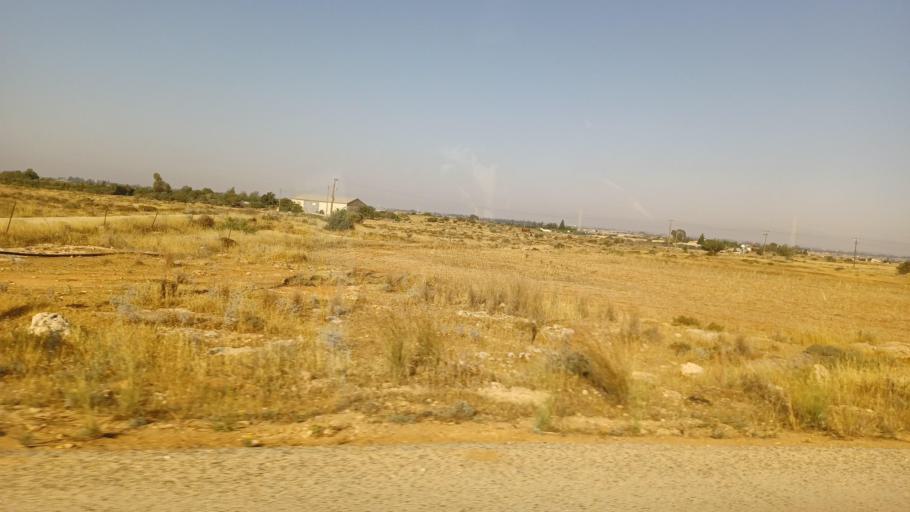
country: CY
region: Ammochostos
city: Frenaros
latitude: 35.0619
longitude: 33.9037
